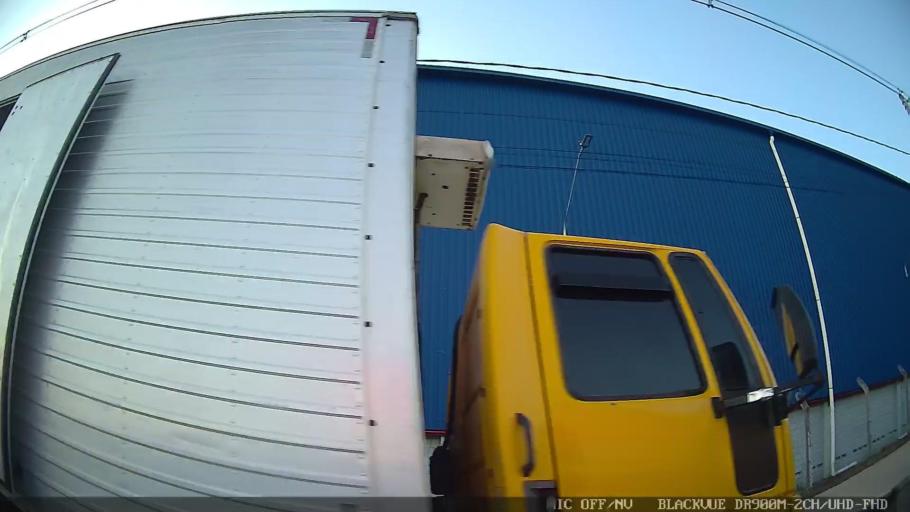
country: BR
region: Sao Paulo
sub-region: Itupeva
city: Itupeva
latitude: -23.2463
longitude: -47.0479
